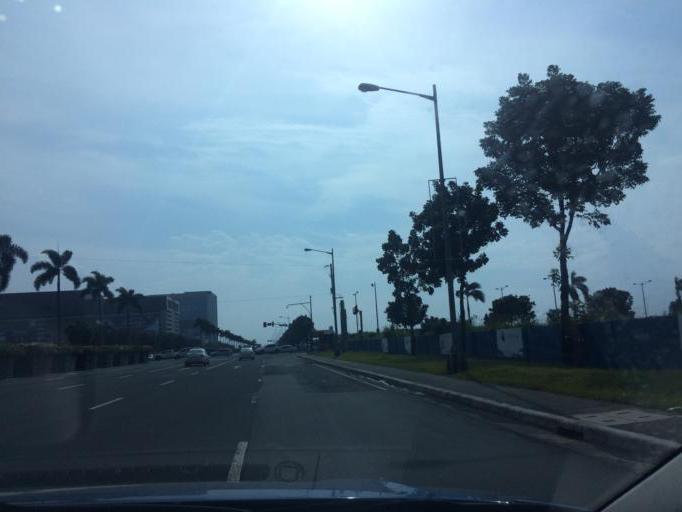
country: PH
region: Metro Manila
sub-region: Makati City
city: Makati City
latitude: 14.5248
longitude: 120.9863
